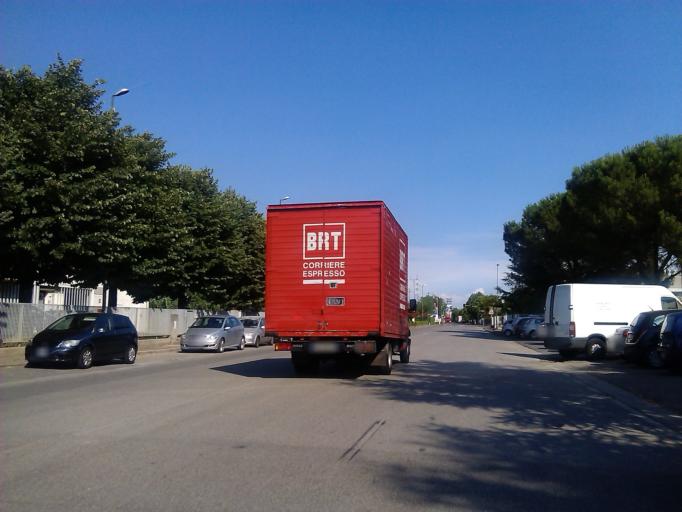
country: IT
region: Tuscany
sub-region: Province of Florence
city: Campi Bisenzio
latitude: 43.8503
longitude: 11.1294
